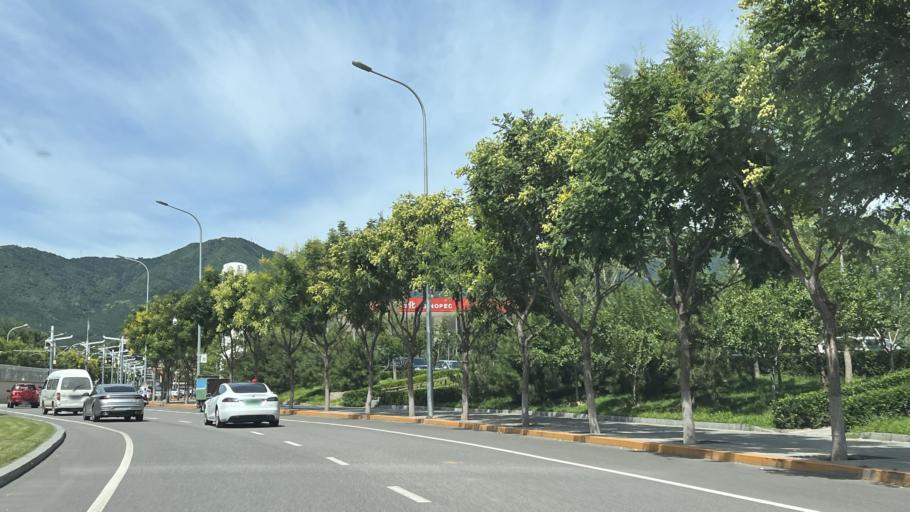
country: CN
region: Beijing
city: Xiangshan
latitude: 39.9926
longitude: 116.2133
